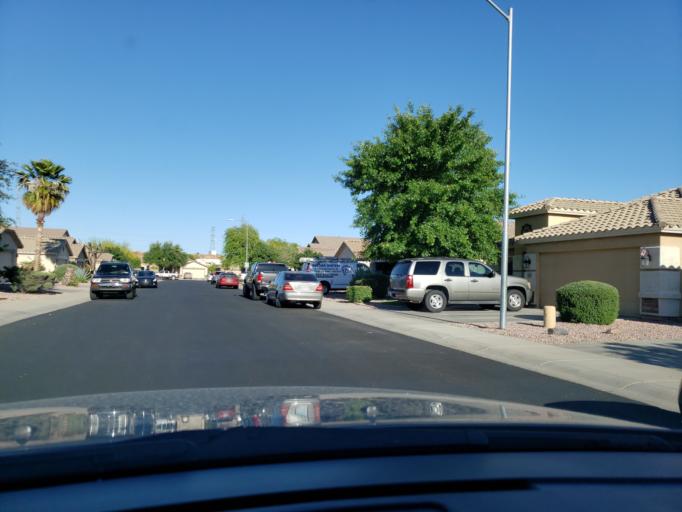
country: US
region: Arizona
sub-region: Maricopa County
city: Youngtown
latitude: 33.5708
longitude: -112.3089
